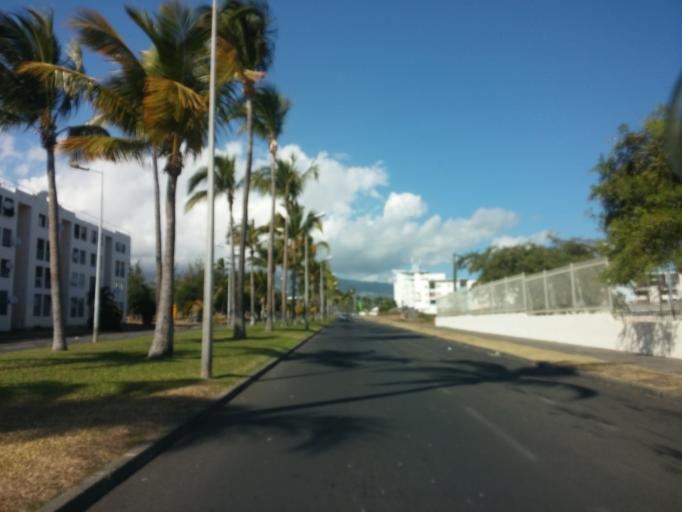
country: RE
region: Reunion
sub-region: Reunion
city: Le Port
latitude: -20.9436
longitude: 55.2924
